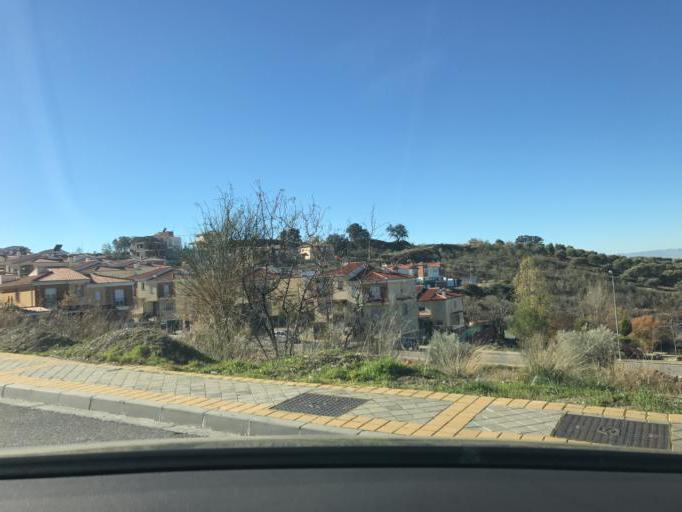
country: ES
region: Andalusia
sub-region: Provincia de Granada
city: Jun
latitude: 37.2185
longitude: -3.5769
